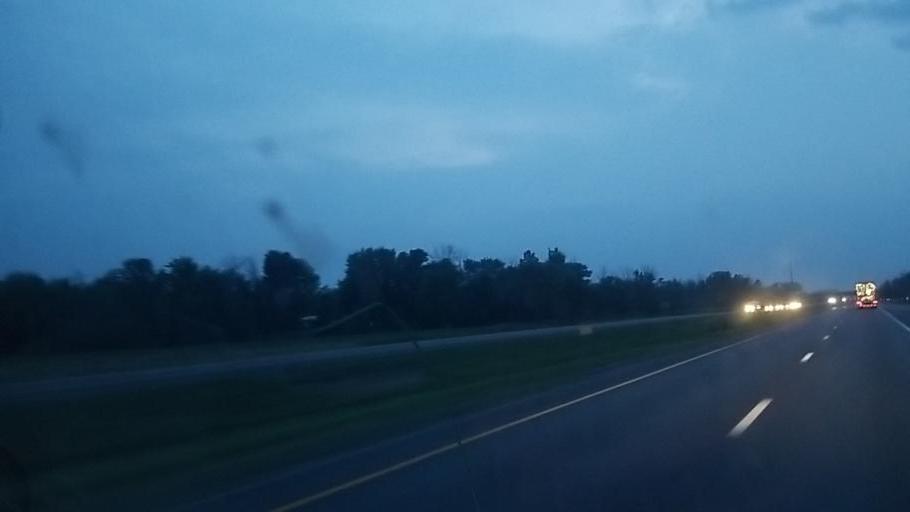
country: US
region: New York
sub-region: Onondaga County
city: East Syracuse
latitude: 43.0949
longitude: -76.0454
